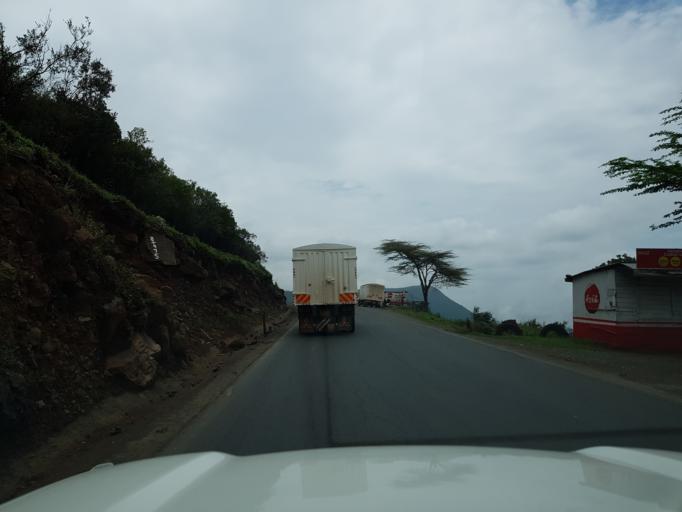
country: KE
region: Kiambu
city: Limuru
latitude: -1.0507
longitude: 36.6019
